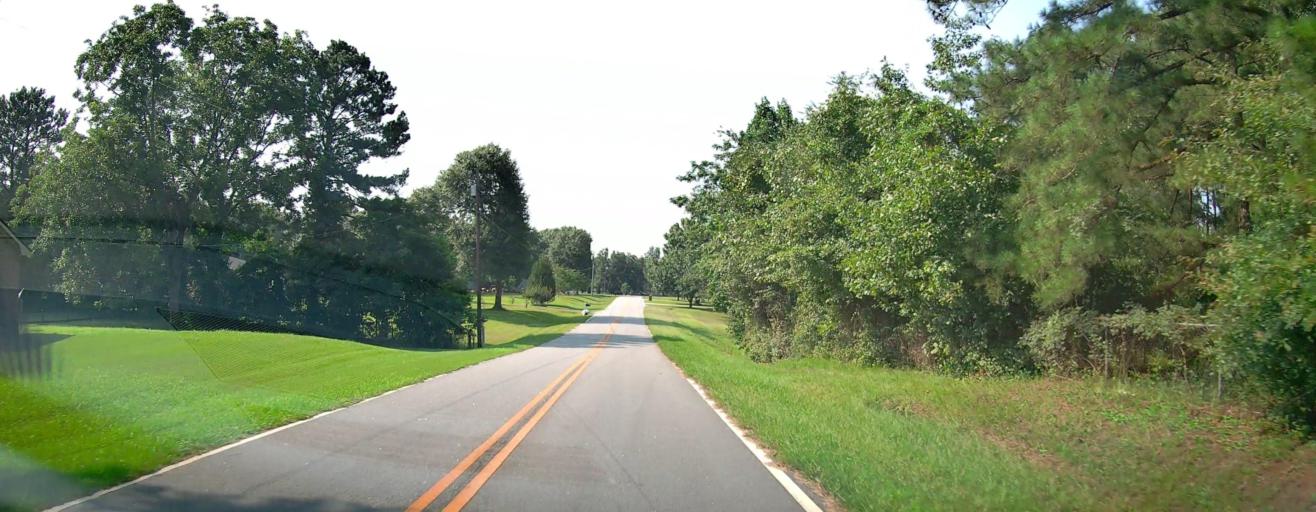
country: US
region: Georgia
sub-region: Houston County
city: Centerville
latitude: 32.6509
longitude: -83.6926
